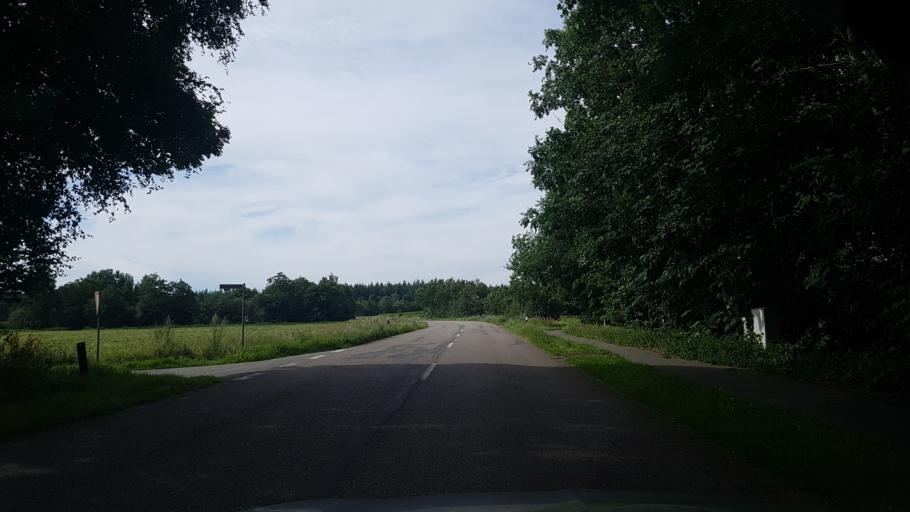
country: DE
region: Schleswig-Holstein
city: Bramstedtlund
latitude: 54.8642
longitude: 9.0489
